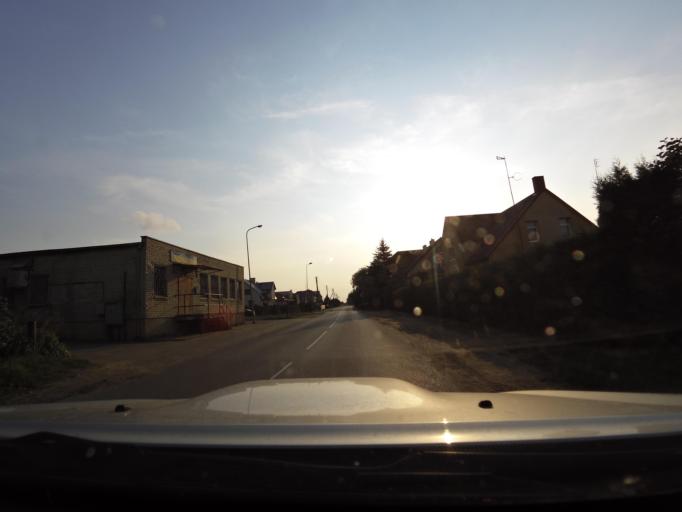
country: LT
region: Klaipedos apskritis
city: Silute
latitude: 55.3424
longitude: 21.4558
